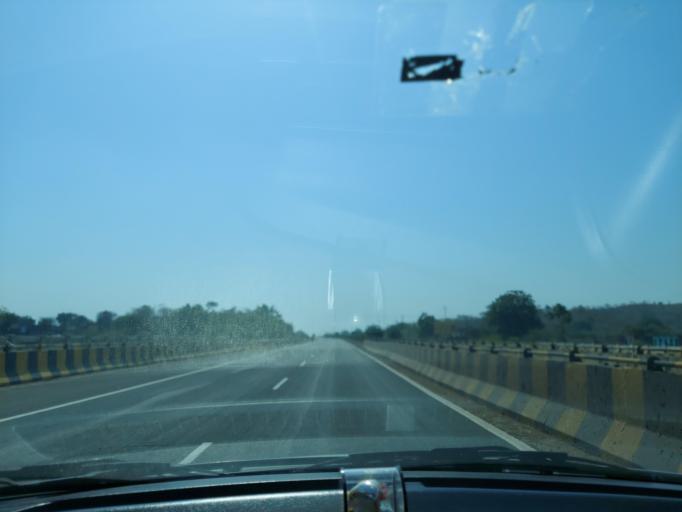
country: IN
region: Madhya Pradesh
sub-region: Dhar
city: Dhamnod
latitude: 22.3110
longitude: 75.5028
